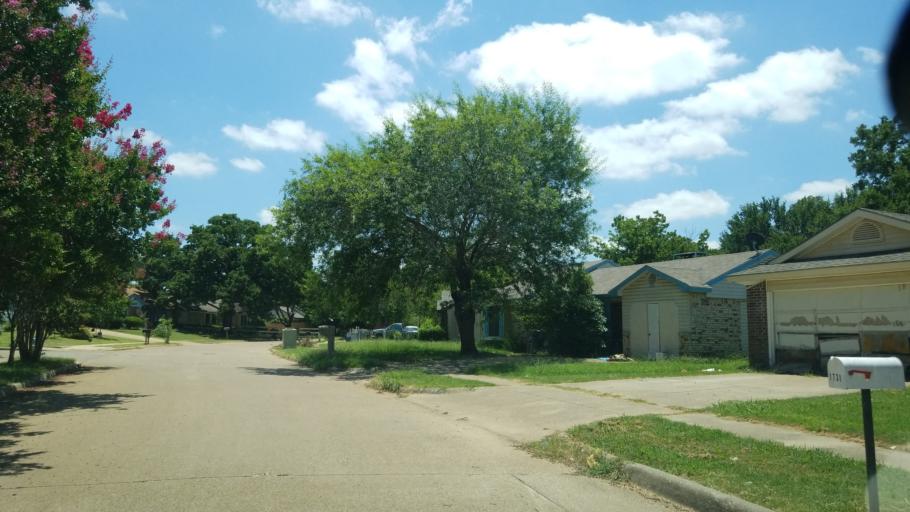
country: US
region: Texas
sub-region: Dallas County
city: Balch Springs
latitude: 32.7428
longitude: -96.7063
